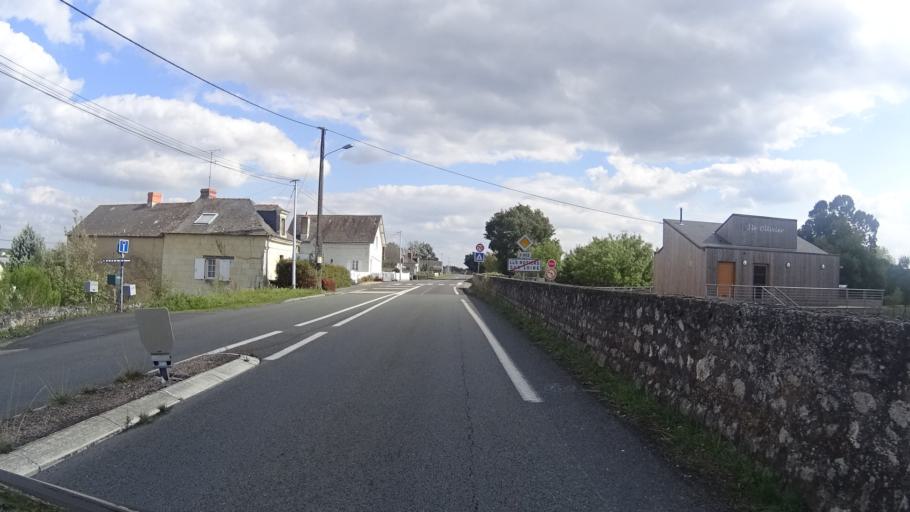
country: FR
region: Pays de la Loire
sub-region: Departement de Maine-et-Loire
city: Les Rosiers-sur-Loire
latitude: 47.3470
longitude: -0.2186
